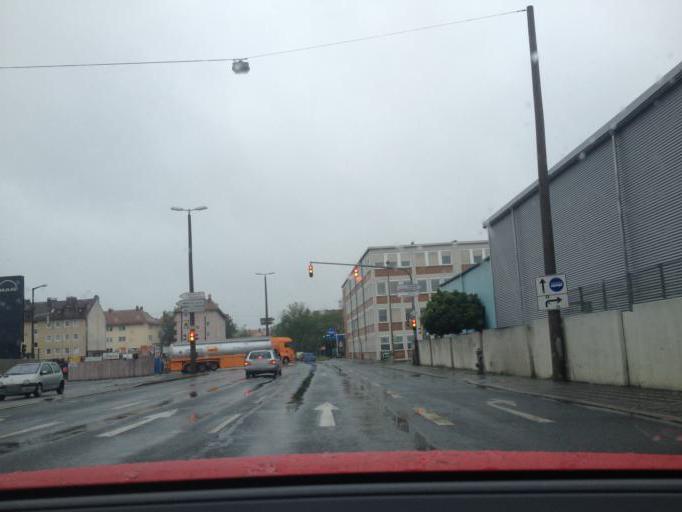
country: DE
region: Bavaria
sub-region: Regierungsbezirk Mittelfranken
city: Nuernberg
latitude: 49.4299
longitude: 11.0726
